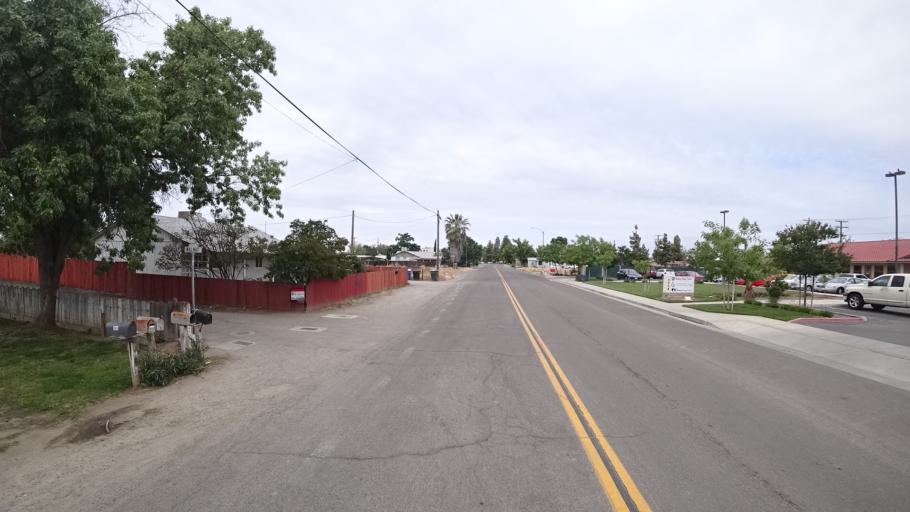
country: US
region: California
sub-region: Kings County
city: Hanford
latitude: 36.3240
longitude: -119.6622
